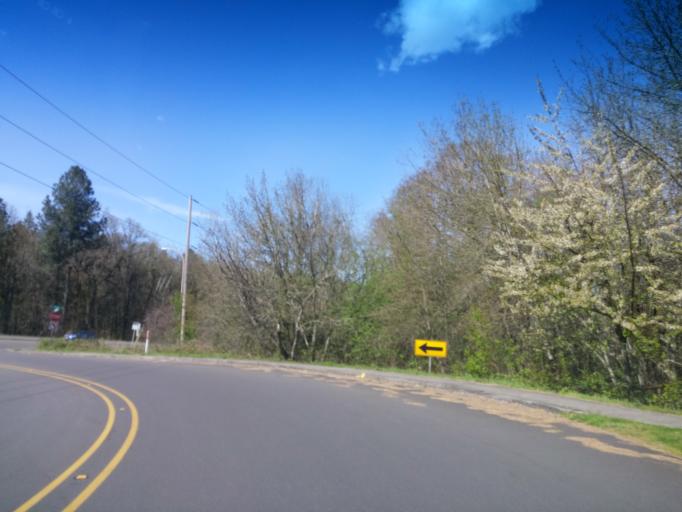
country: US
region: Oregon
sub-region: Washington County
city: Beaverton
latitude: 45.4999
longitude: -122.8279
